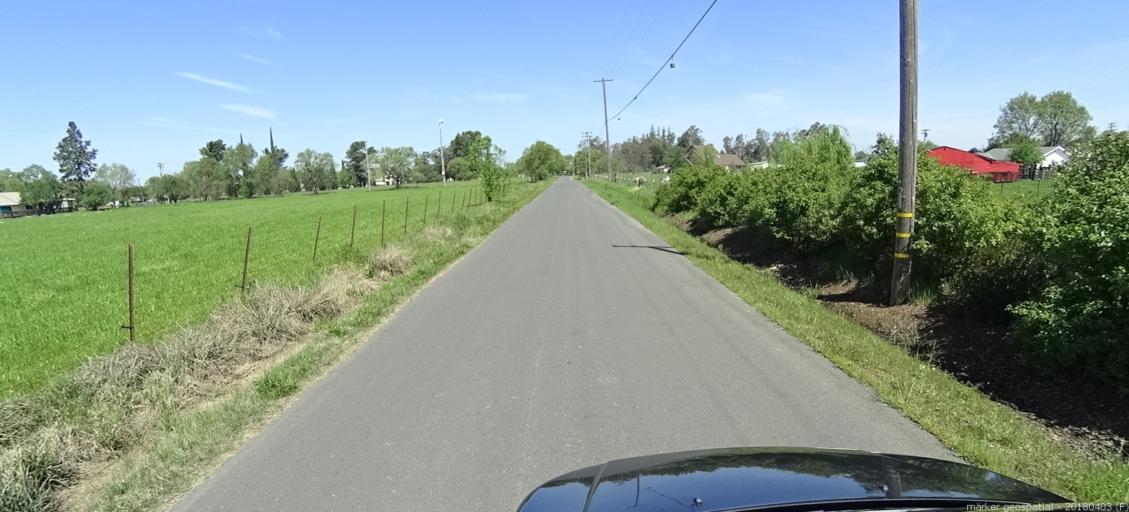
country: US
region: California
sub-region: Sacramento County
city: Wilton
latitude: 38.4011
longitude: -121.2782
